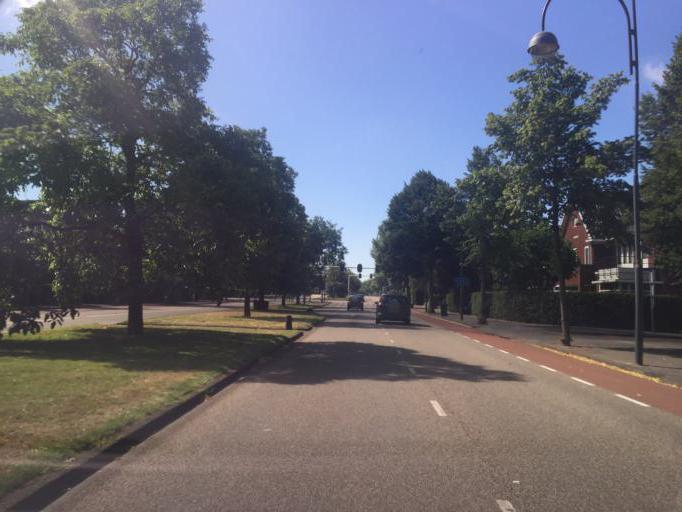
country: NL
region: North Holland
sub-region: Gemeente Heemstede
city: Heemstede
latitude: 52.3511
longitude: 4.6243
